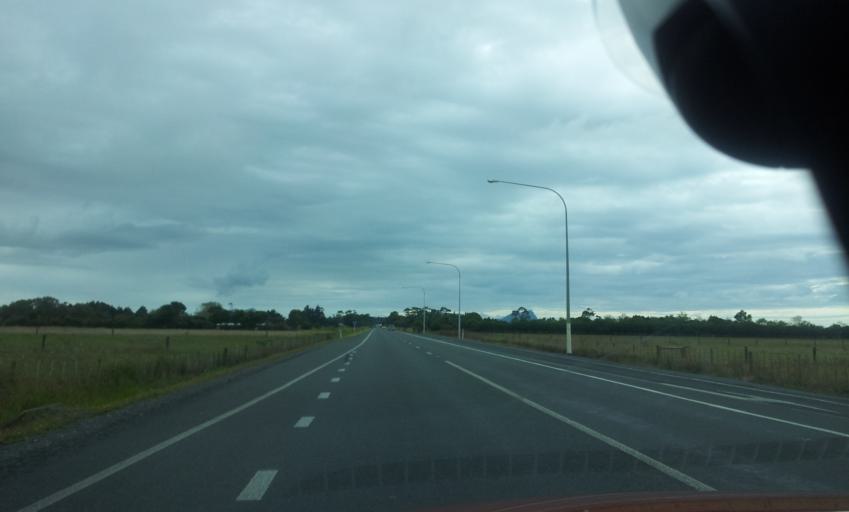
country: NZ
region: Northland
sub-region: Whangarei
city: Ruakaka
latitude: -35.9779
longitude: 174.4355
